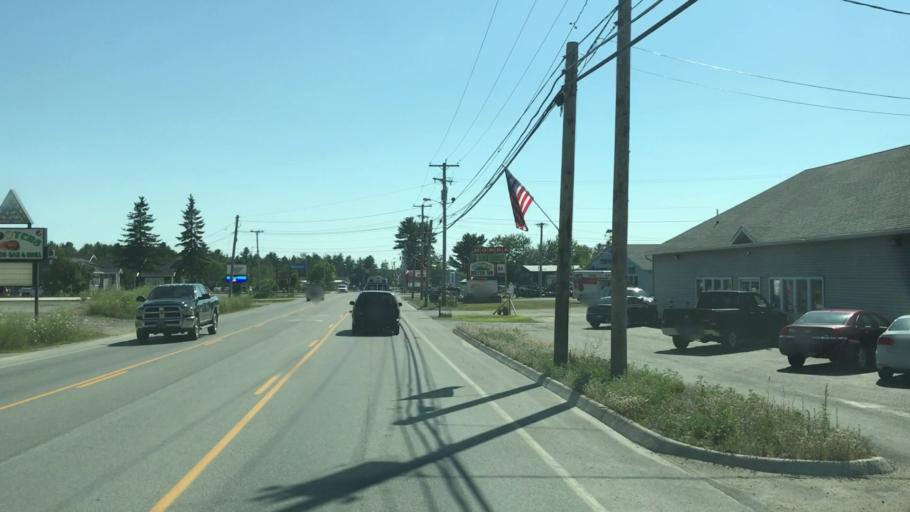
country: US
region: Maine
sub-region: Penobscot County
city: Lincoln
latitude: 45.3585
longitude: -68.5239
